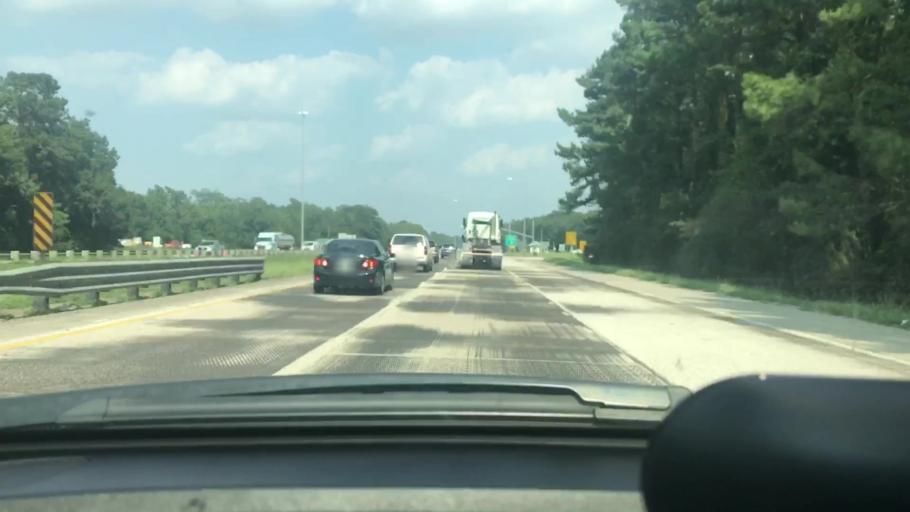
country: US
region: Louisiana
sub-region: Livingston Parish
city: Albany
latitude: 30.4793
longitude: -90.5249
